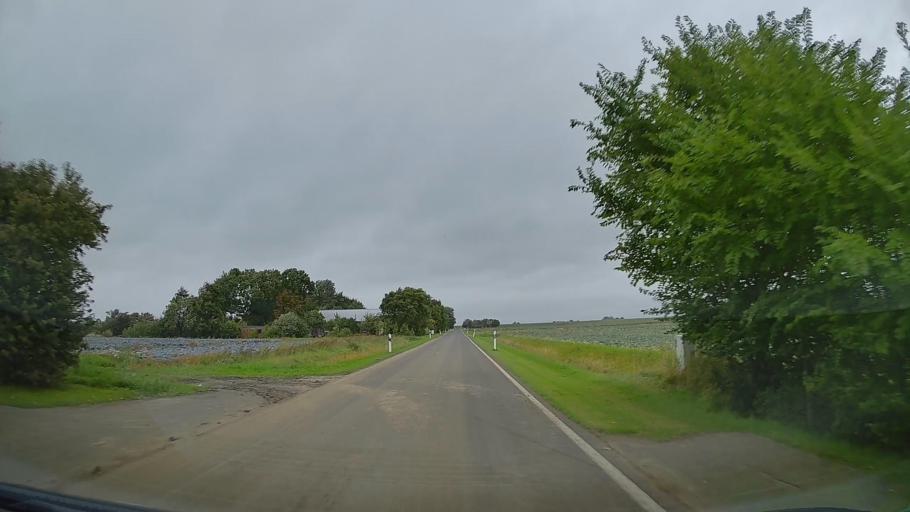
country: DE
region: Schleswig-Holstein
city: Friedrichskoog
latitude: 54.0187
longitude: 8.9095
